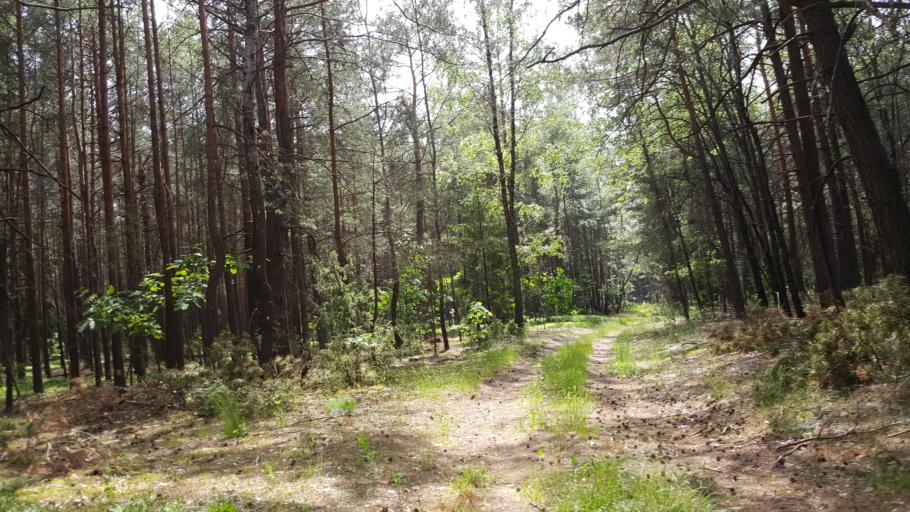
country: BY
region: Brest
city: Kamyanyets
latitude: 52.4798
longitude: 23.8427
